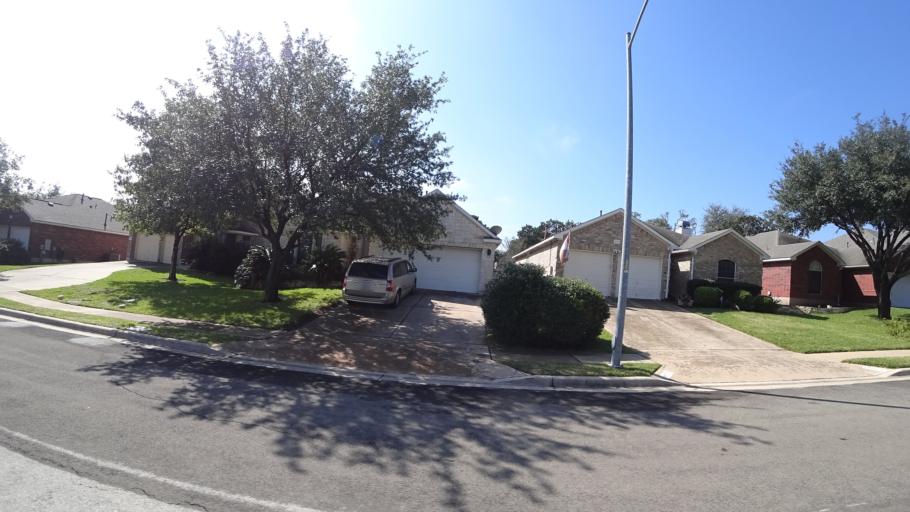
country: US
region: Texas
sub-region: Travis County
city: Shady Hollow
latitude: 30.2064
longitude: -97.8724
